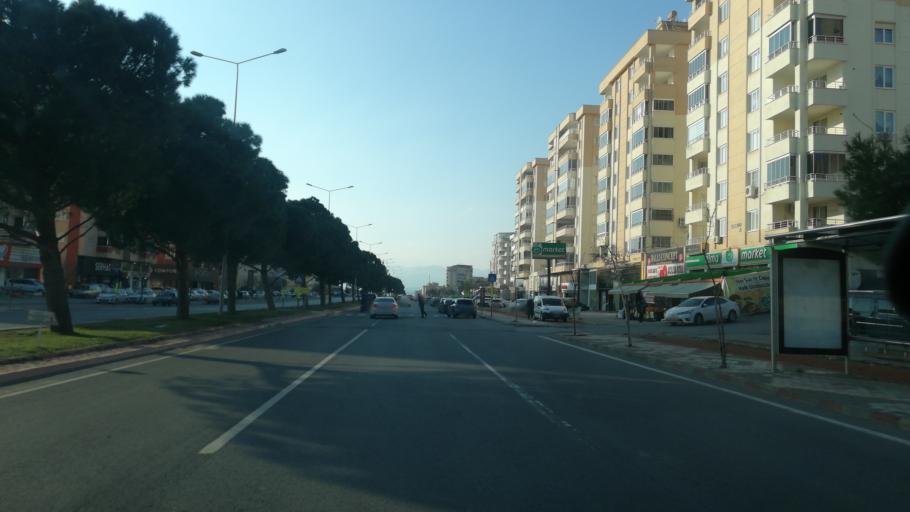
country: TR
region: Kahramanmaras
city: Kahramanmaras
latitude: 37.5948
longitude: 36.8542
